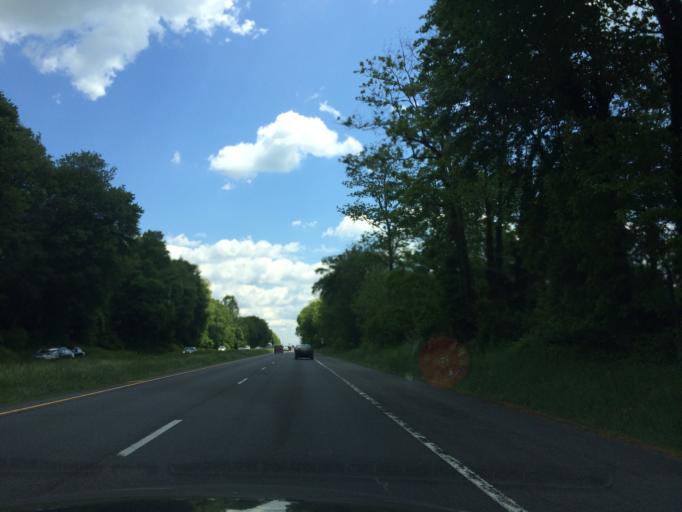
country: US
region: Maryland
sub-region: Howard County
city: Columbia
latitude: 39.2787
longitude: -76.8509
